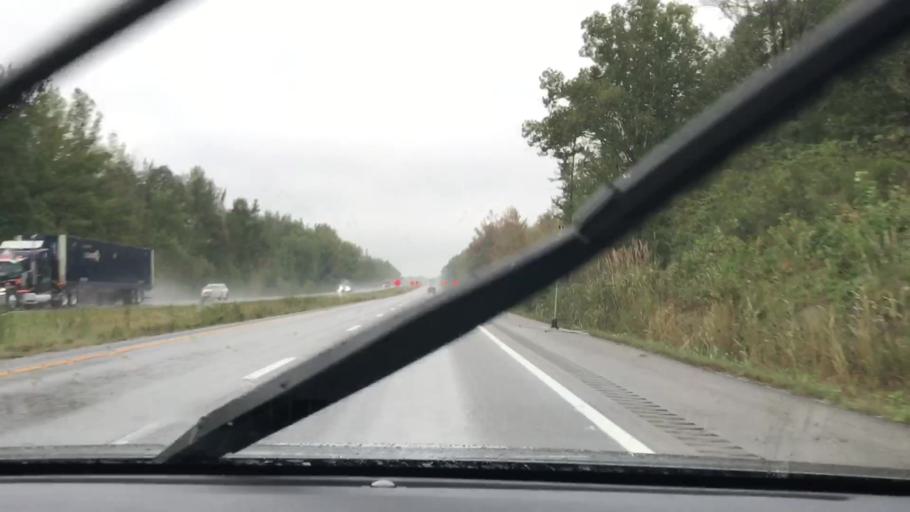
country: US
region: Kentucky
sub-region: Hopkins County
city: Nortonville
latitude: 37.1637
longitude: -87.4560
